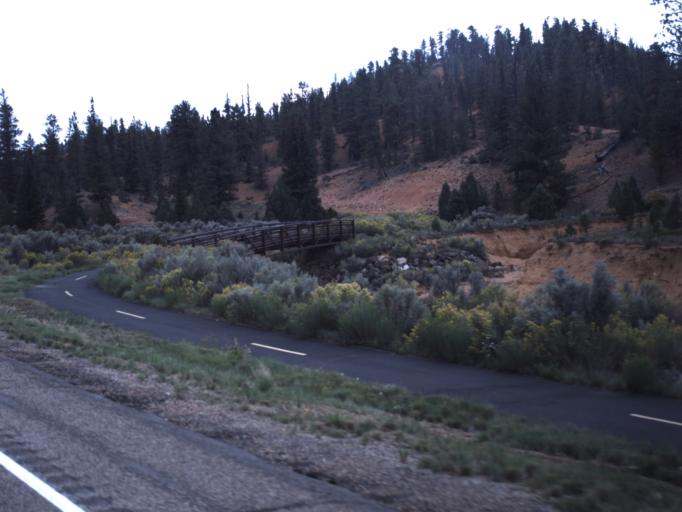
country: US
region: Utah
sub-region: Garfield County
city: Panguitch
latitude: 37.7361
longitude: -112.2871
